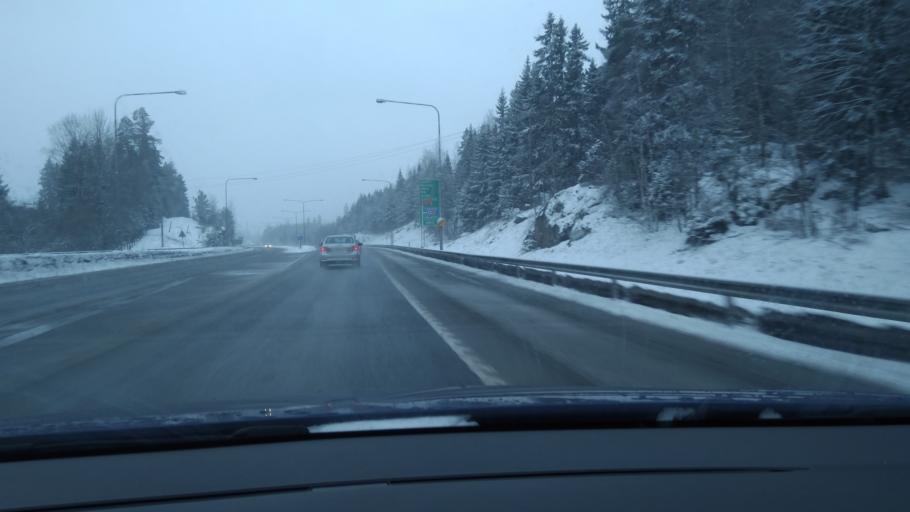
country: FI
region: Pirkanmaa
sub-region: Tampere
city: Tampere
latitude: 61.5060
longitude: 23.9010
